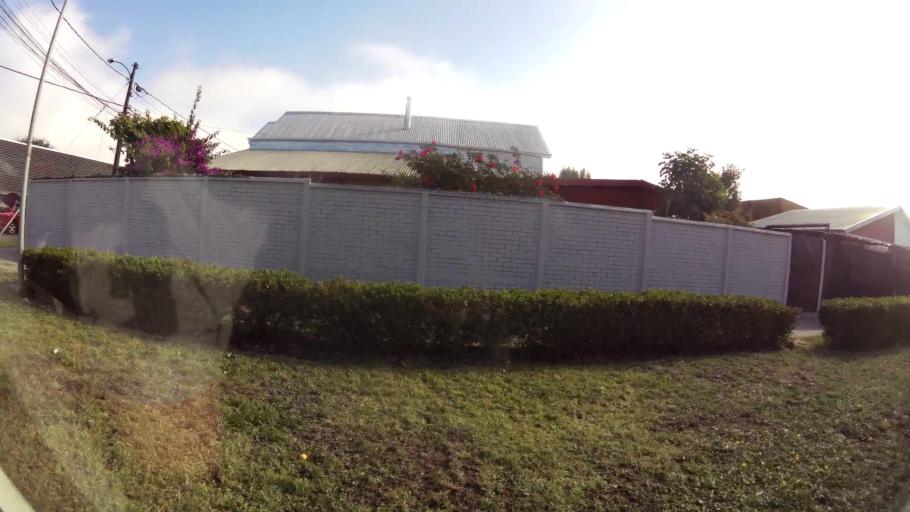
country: CL
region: Biobio
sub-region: Provincia de Concepcion
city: Concepcion
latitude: -36.7955
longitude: -73.0998
